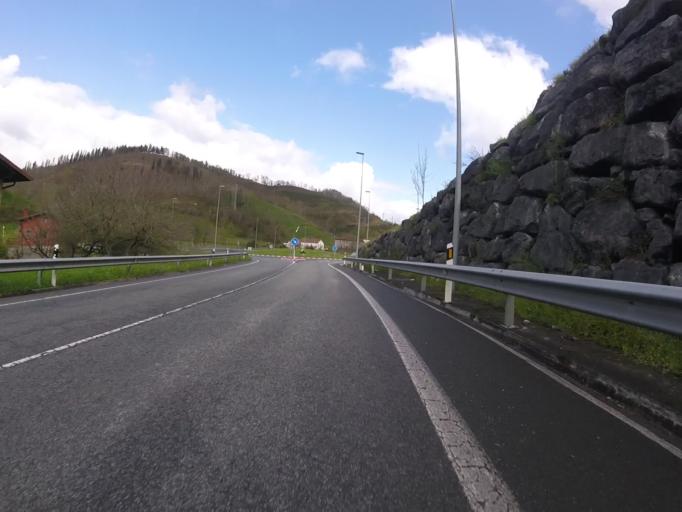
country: ES
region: Basque Country
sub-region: Provincia de Guipuzcoa
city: Amezqueta
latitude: 43.0526
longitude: -2.0882
